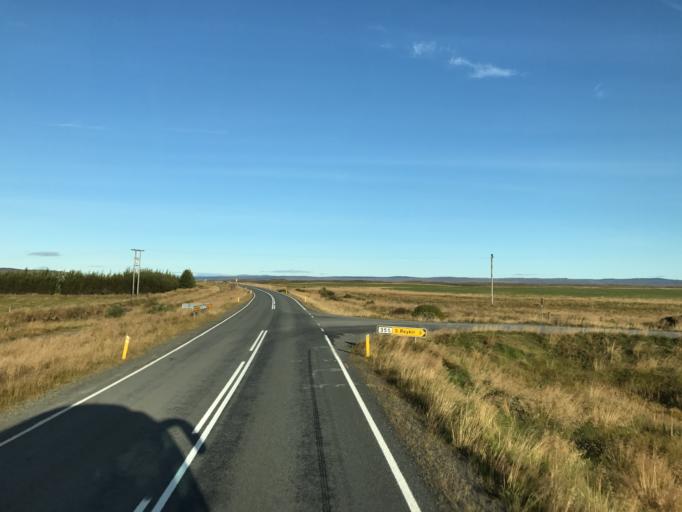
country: IS
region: South
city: Selfoss
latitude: 64.2400
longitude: -20.5185
